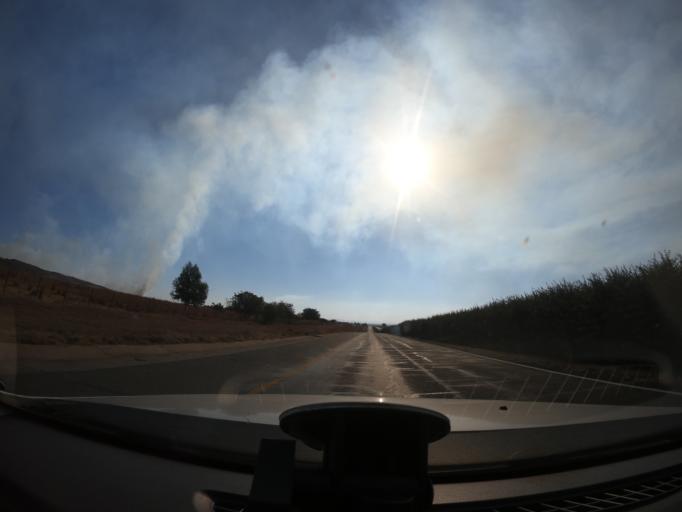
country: ZA
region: Gauteng
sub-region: Sedibeng District Municipality
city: Heidelberg
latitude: -26.4596
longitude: 28.3290
